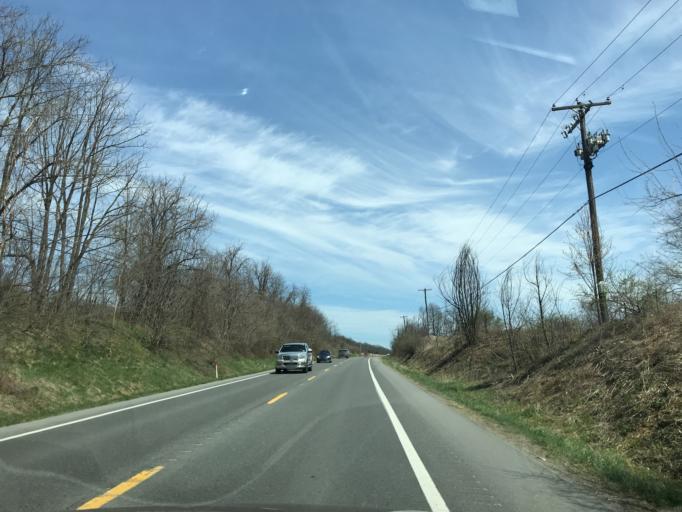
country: US
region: Pennsylvania
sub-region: Snyder County
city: Middleburg
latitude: 40.8064
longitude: -76.9558
